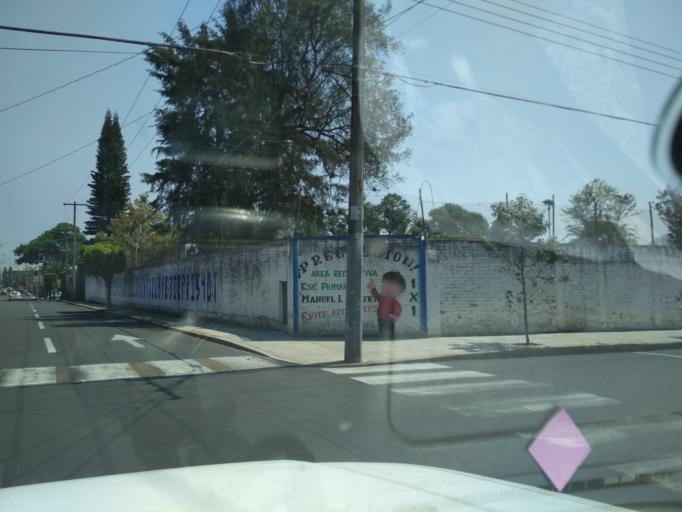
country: MX
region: Veracruz
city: Orizaba
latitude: 18.8552
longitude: -97.0937
